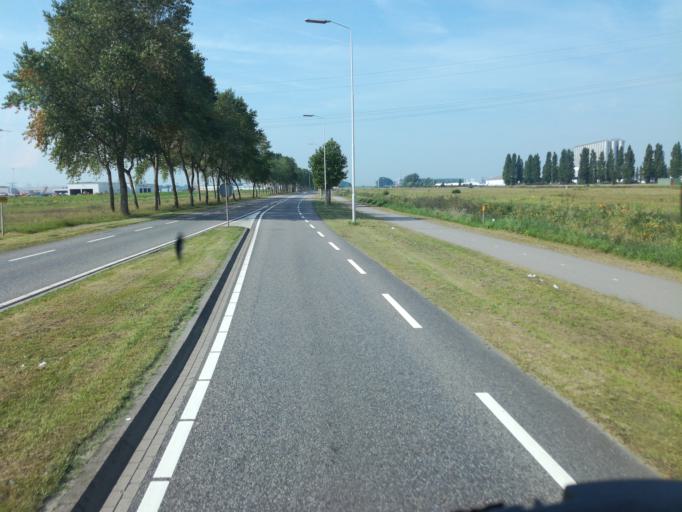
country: NL
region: North Brabant
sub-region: Gemeente Moerdijk
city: Klundert
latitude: 51.6662
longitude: 4.5831
